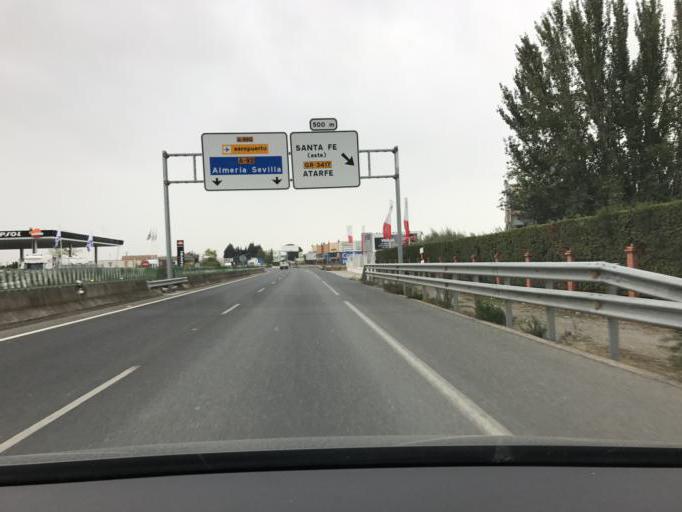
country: ES
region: Andalusia
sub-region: Provincia de Granada
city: Atarfe
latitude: 37.1931
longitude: -3.6977
